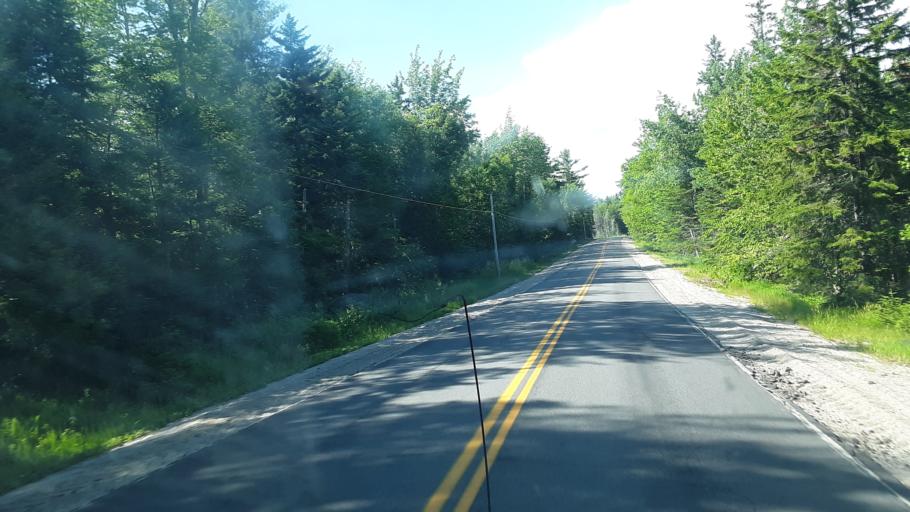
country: US
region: Maine
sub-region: Washington County
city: Cherryfield
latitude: 44.7772
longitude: -68.0344
